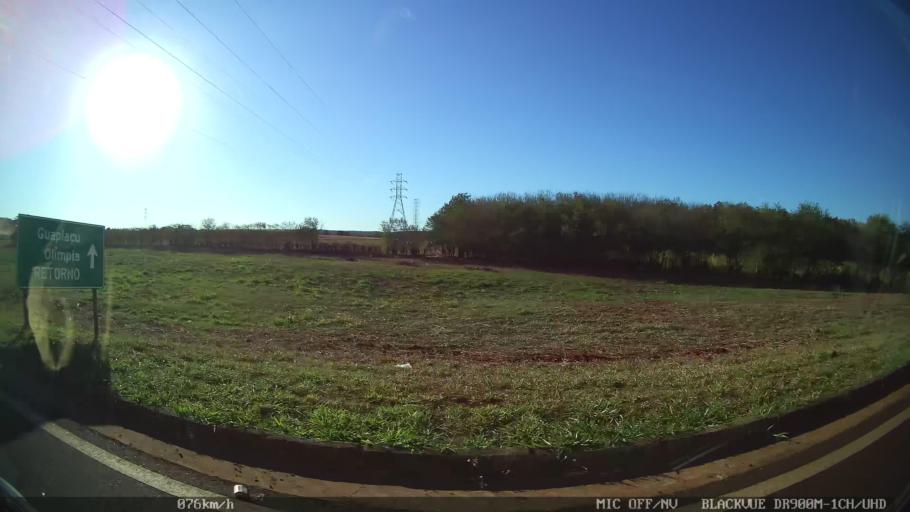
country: BR
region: Sao Paulo
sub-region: Guapiacu
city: Guapiacu
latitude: -20.7721
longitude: -49.2233
